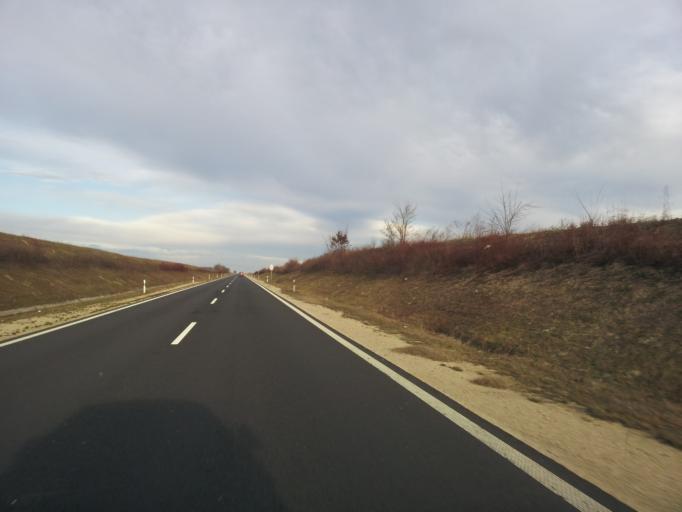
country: HU
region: Veszprem
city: Balatonkenese
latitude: 47.0266
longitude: 18.1773
